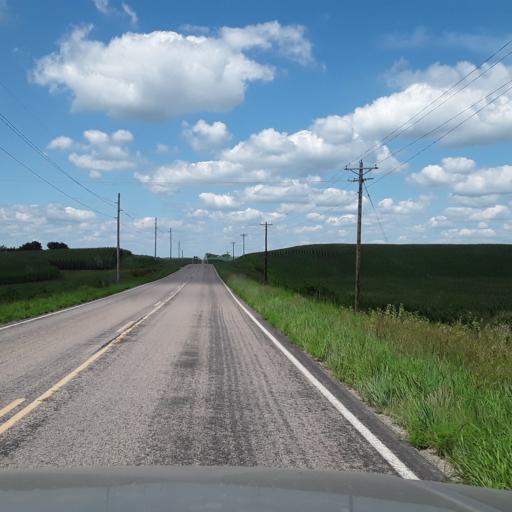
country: US
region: Nebraska
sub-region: Nance County
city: Genoa
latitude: 41.5338
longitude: -97.6960
